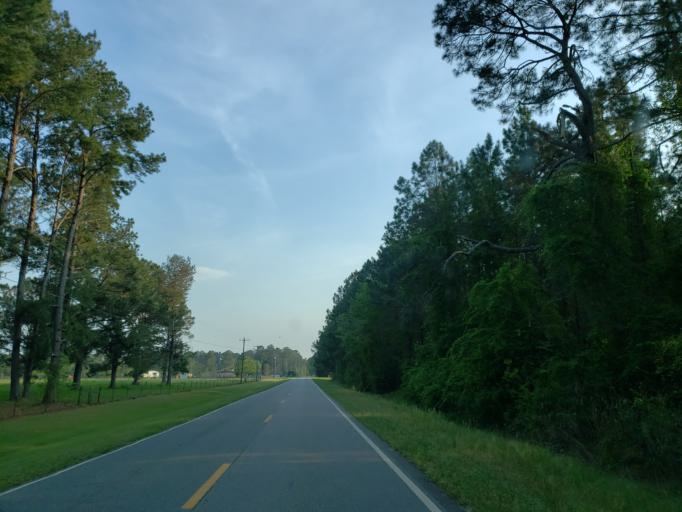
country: US
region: Georgia
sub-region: Cook County
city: Sparks
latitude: 31.1885
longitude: -83.4273
